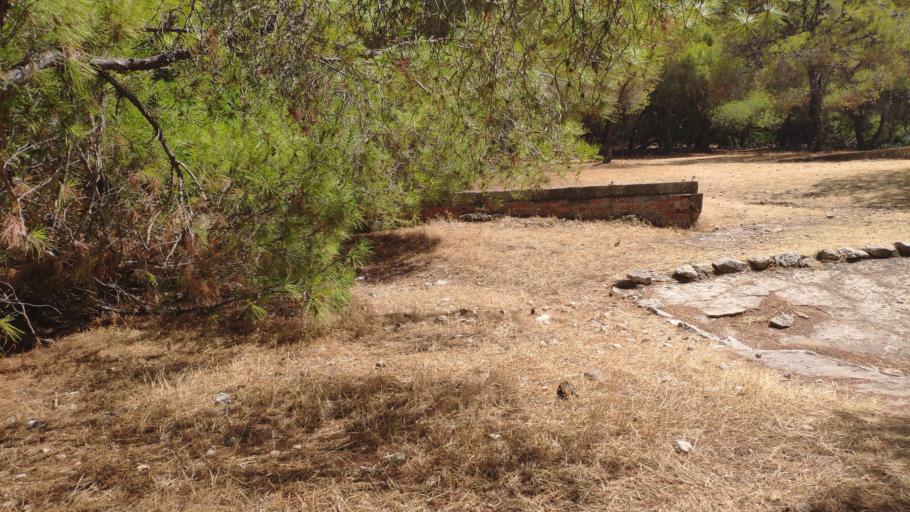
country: GR
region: Attica
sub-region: Nomos Piraios
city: Aegina
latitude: 37.6948
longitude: 23.4340
